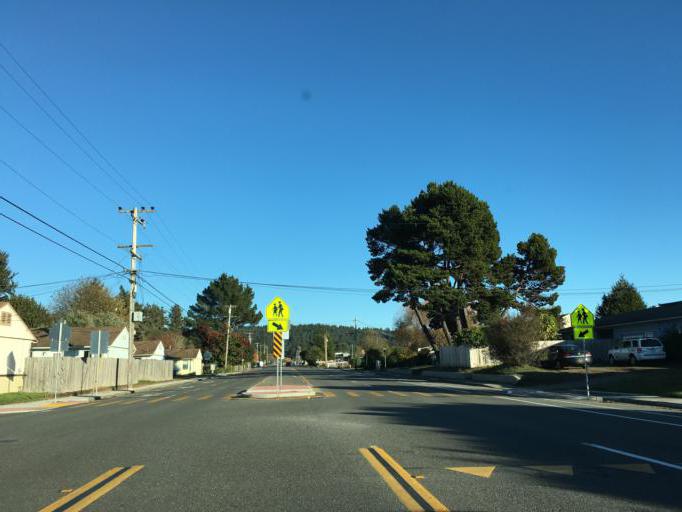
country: US
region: California
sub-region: Humboldt County
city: McKinleyville
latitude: 40.9562
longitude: -124.1058
